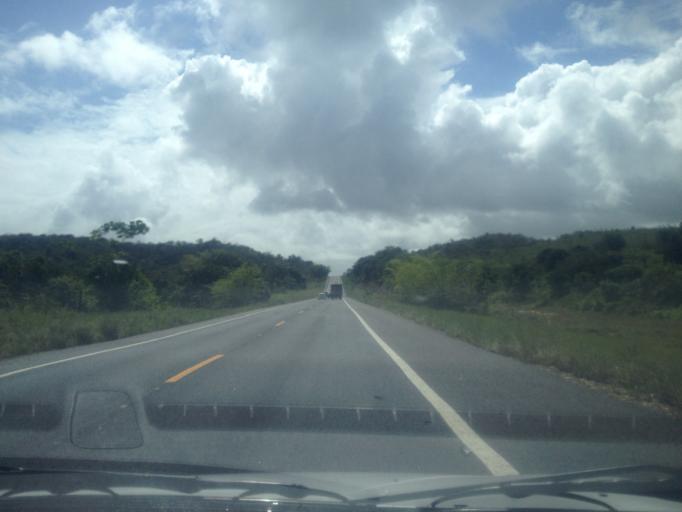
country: BR
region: Sergipe
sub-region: Indiaroba
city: Indiaroba
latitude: -11.5935
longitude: -37.5425
